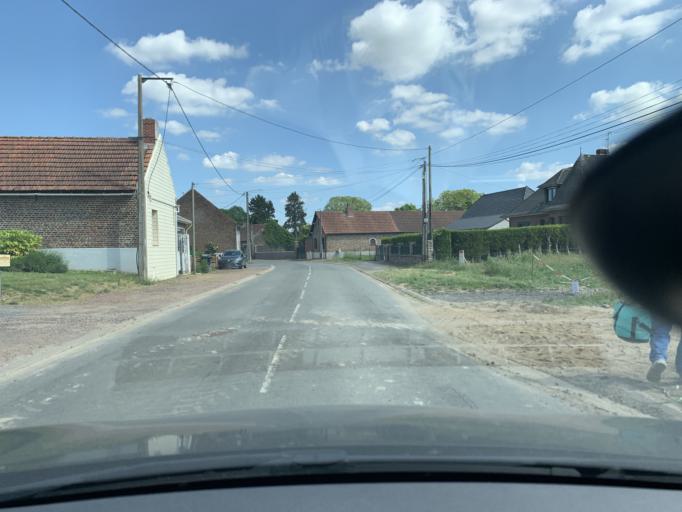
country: FR
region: Nord-Pas-de-Calais
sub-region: Departement du Pas-de-Calais
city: Marquion
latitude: 50.2342
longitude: 3.0941
